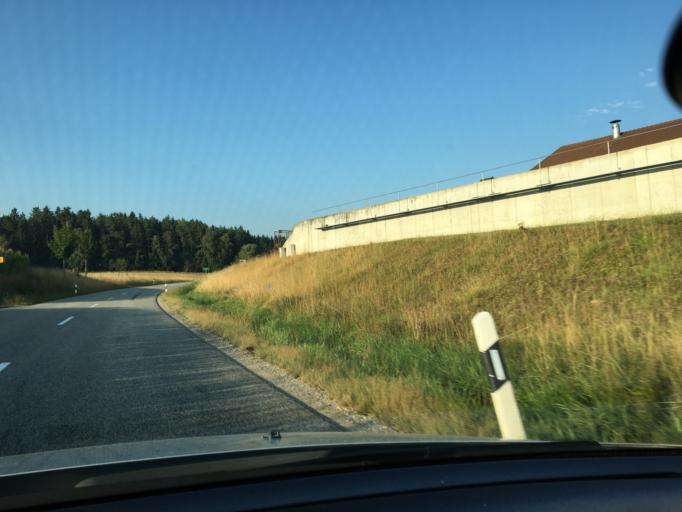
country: DE
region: Bavaria
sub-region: Lower Bavaria
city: Aham
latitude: 48.4906
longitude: 12.4654
